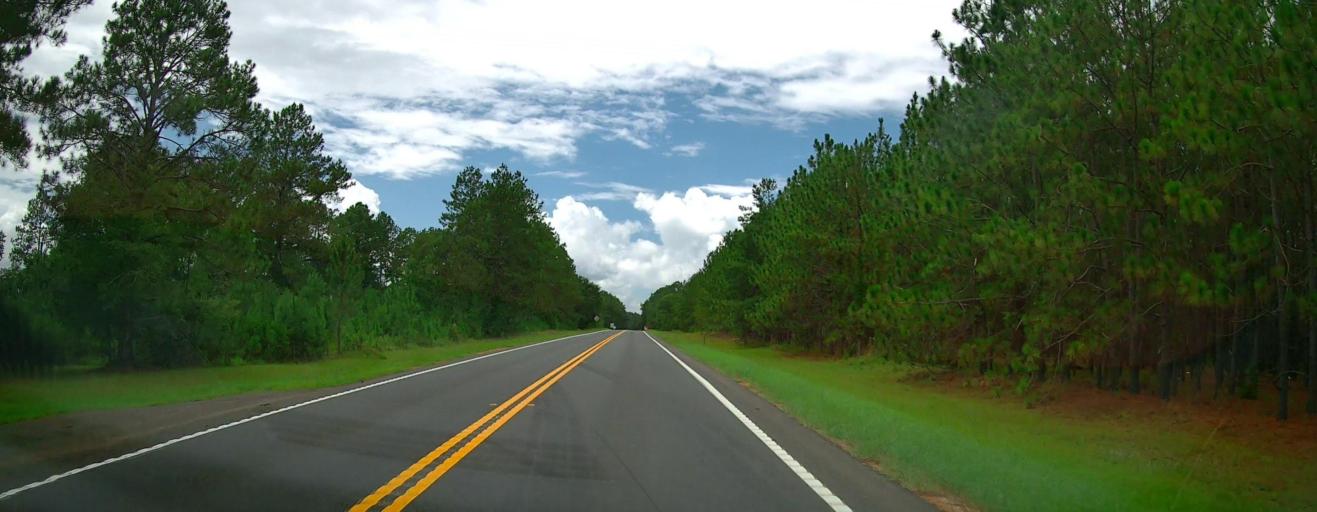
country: US
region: Georgia
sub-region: Dooly County
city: Vienna
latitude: 32.0858
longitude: -83.6014
